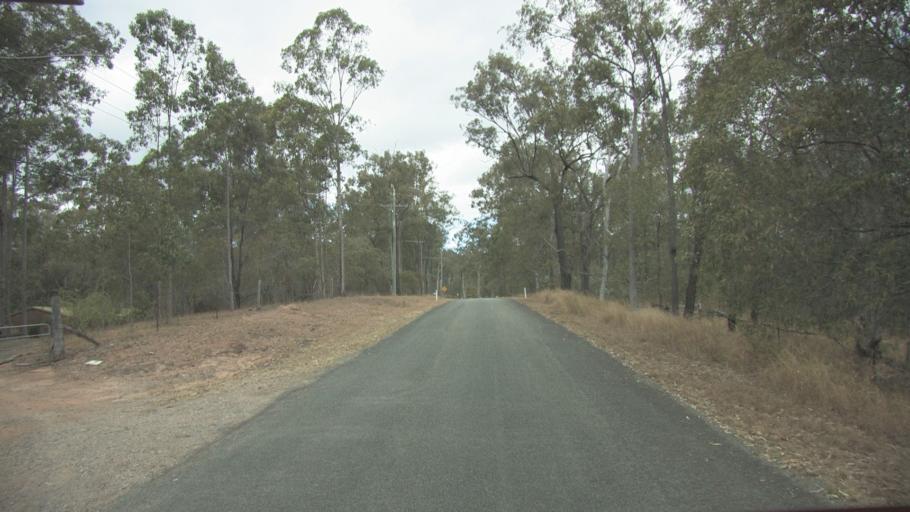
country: AU
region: Queensland
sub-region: Logan
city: Cedar Vale
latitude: -27.8859
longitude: 153.0397
